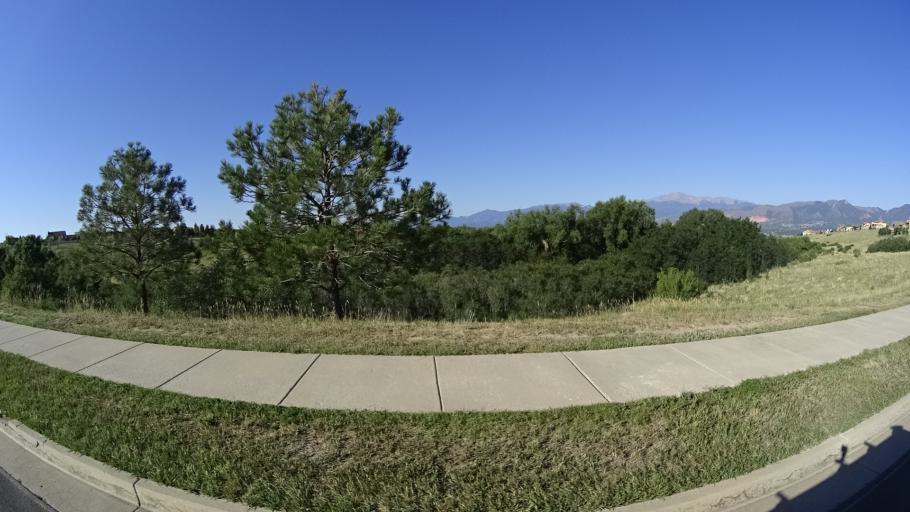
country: US
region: Colorado
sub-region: El Paso County
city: Black Forest
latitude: 38.9736
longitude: -104.7569
